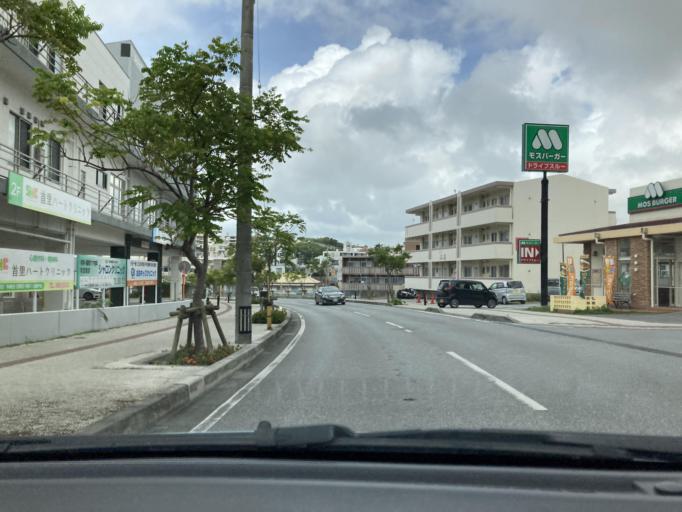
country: JP
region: Okinawa
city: Ginowan
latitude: 26.2342
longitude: 127.7346
